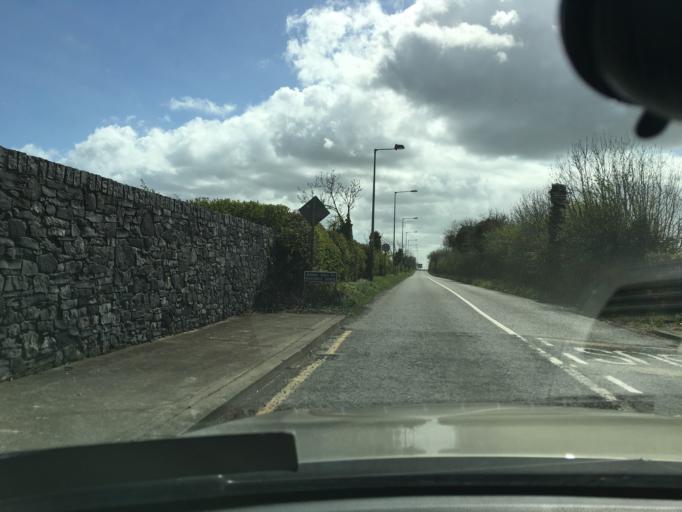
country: IE
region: Leinster
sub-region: Fingal County
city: Blanchardstown
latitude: 53.4267
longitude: -6.3699
